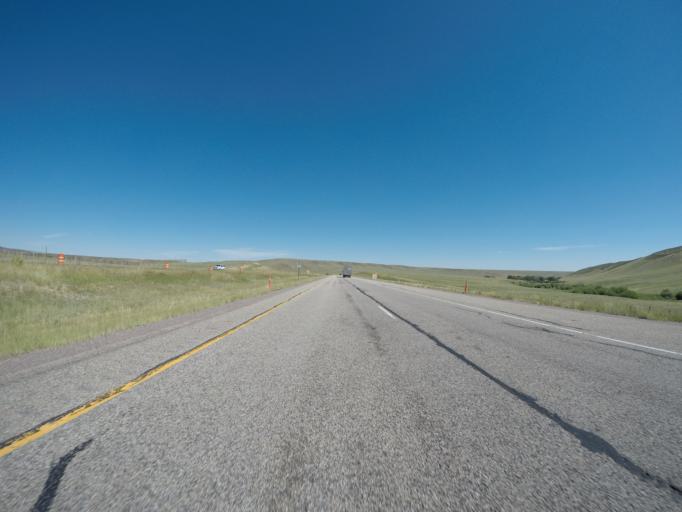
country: US
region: Wyoming
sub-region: Albany County
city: Laramie
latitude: 41.5152
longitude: -106.0550
